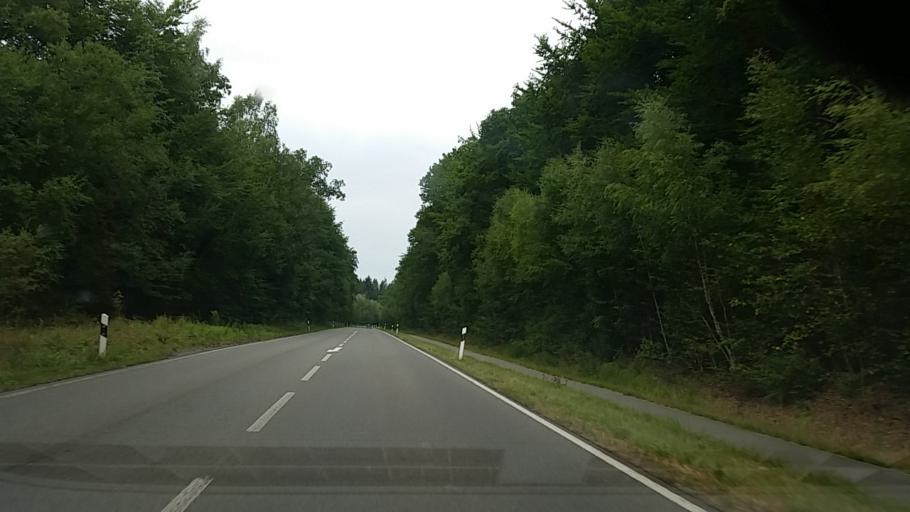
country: DE
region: Schleswig-Holstein
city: Dassendorf
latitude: 53.5108
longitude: 10.3619
